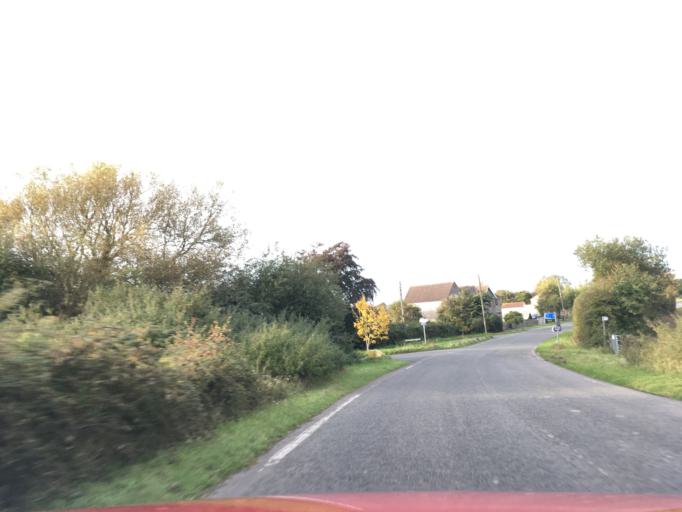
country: GB
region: England
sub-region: South Gloucestershire
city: Severn Beach
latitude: 51.5704
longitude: -2.6372
